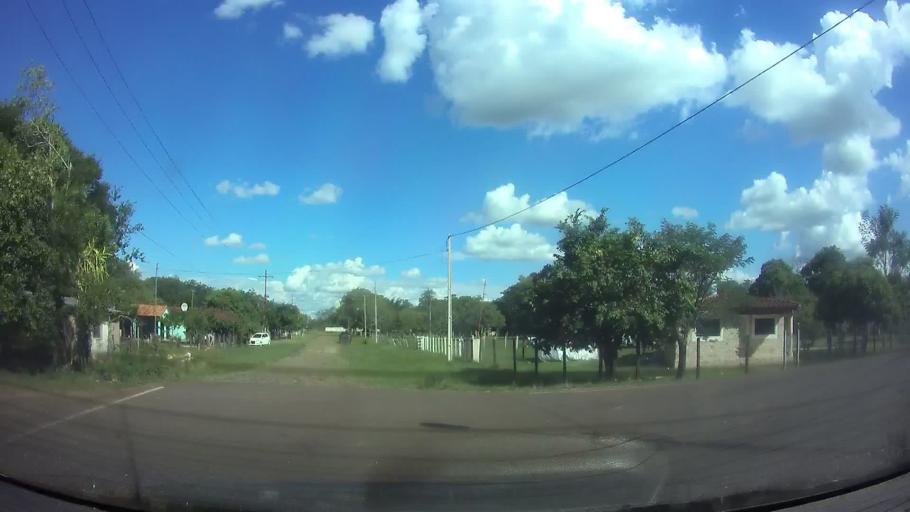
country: PY
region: Paraguari
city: Sapucai
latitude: -25.6878
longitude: -56.8615
